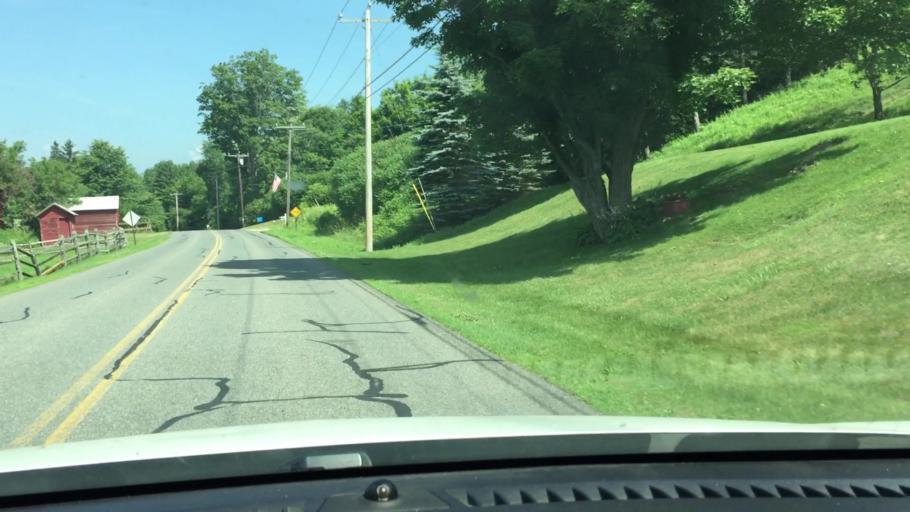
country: US
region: Massachusetts
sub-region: Berkshire County
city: Lee
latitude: 42.2395
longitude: -73.1957
